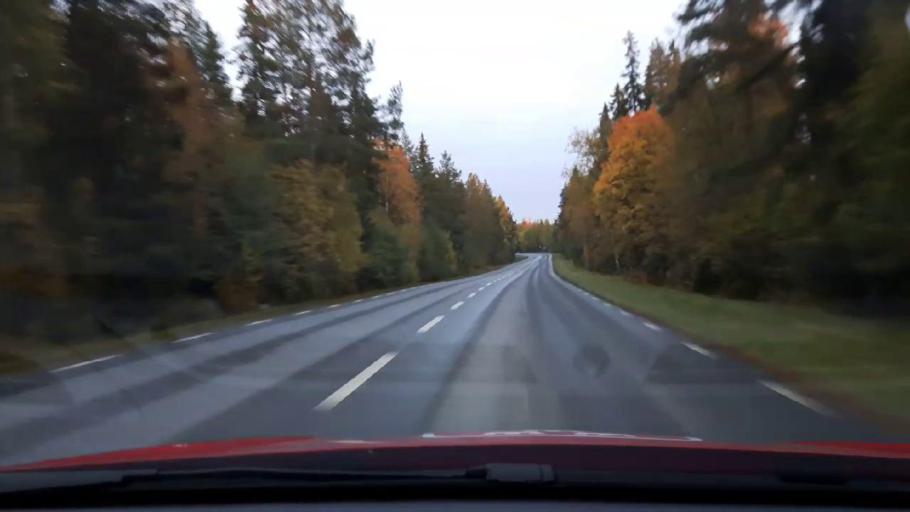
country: SE
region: Jaemtland
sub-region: OEstersunds Kommun
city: Ostersund
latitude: 63.2135
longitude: 14.6235
